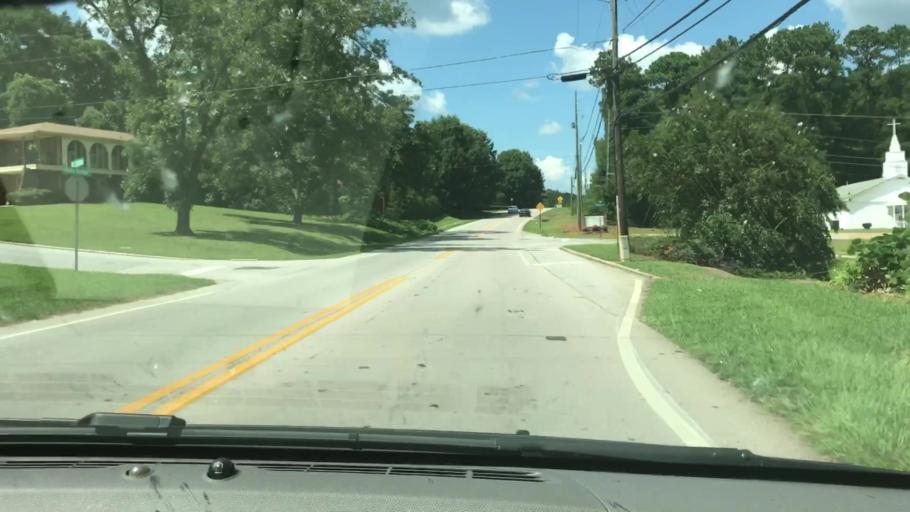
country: US
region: Georgia
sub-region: Troup County
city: La Grange
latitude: 33.0633
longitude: -85.0378
